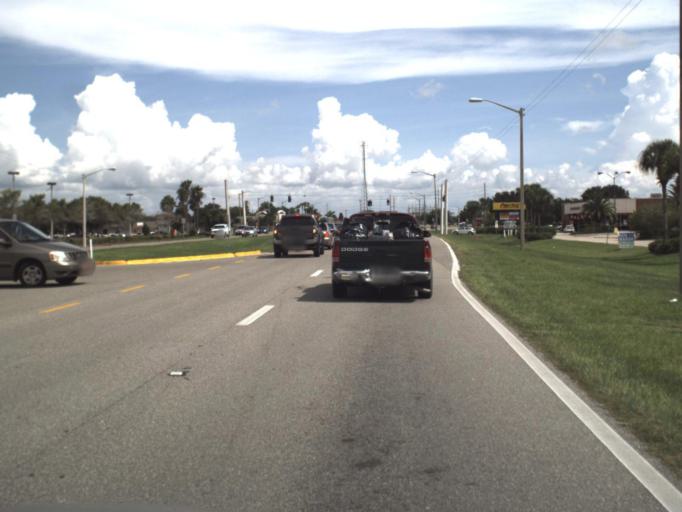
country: US
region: Florida
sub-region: Sarasota County
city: Nokomis
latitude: 27.1073
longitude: -82.4393
